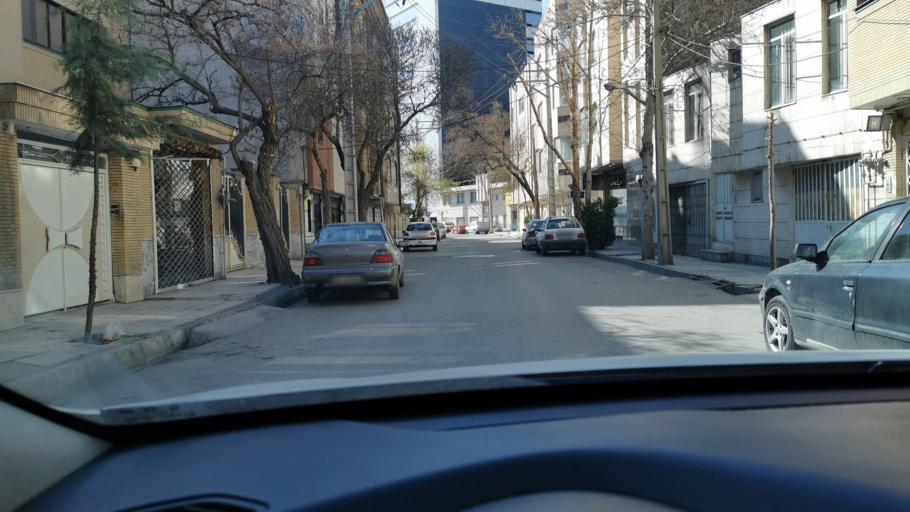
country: IR
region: Razavi Khorasan
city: Mashhad
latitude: 36.2900
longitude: 59.5787
